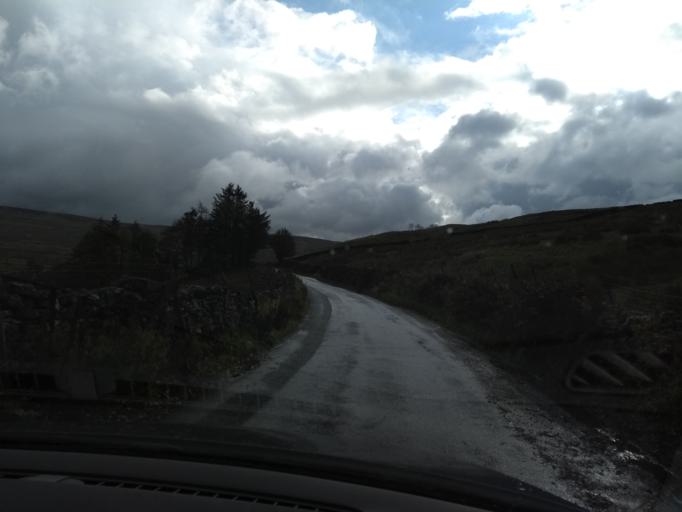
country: GB
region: England
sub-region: Cumbria
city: Kirkby Stephen
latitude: 54.3863
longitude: -2.1733
